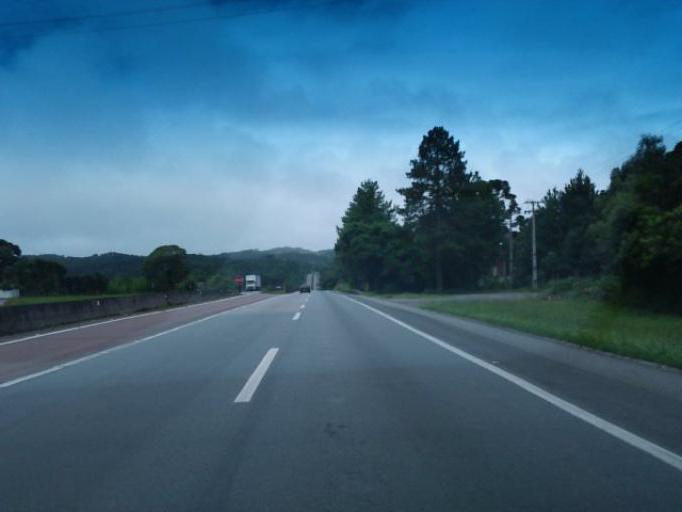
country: BR
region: Parana
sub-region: Campina Grande Do Sul
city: Campina Grande do Sul
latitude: -25.3074
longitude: -48.9786
